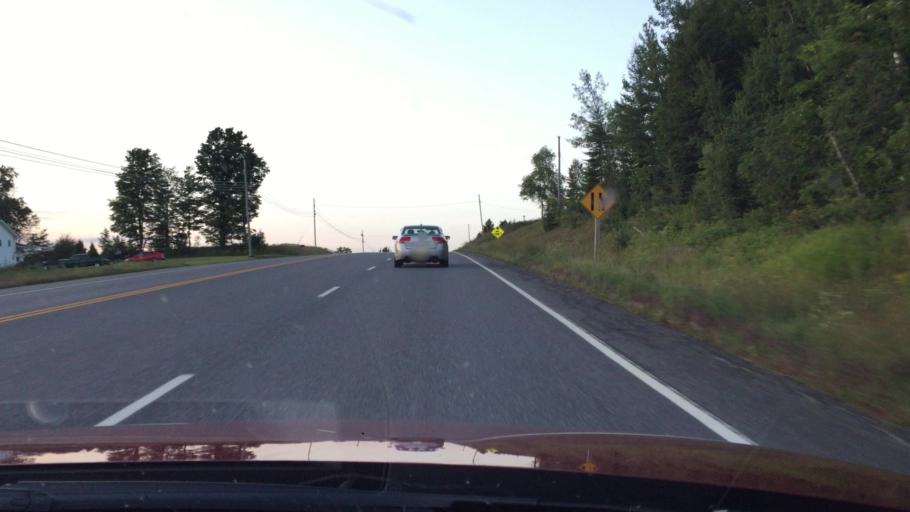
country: CA
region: New Brunswick
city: Florenceville-Bristol
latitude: 46.3896
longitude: -67.8428
